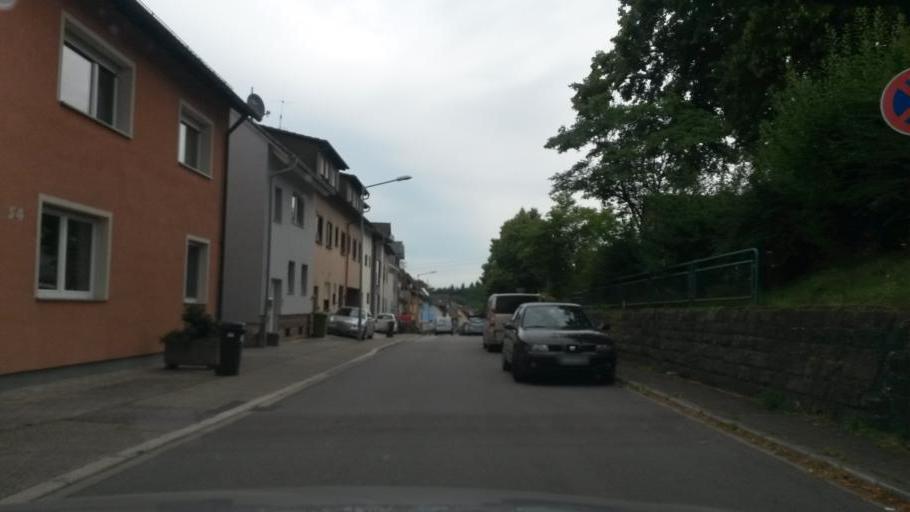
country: DE
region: Baden-Wuerttemberg
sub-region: Karlsruhe Region
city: Konigsbach-Stein
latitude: 48.9149
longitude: 8.5332
